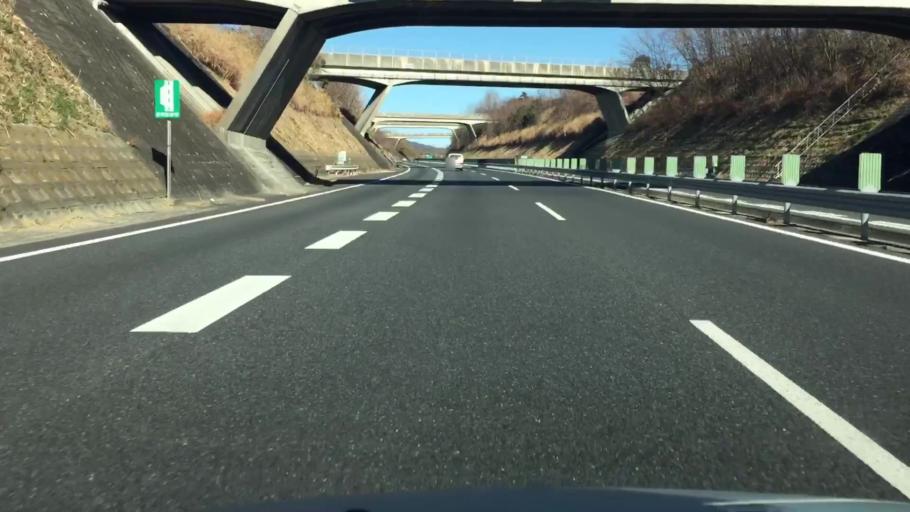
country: JP
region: Gunma
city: Shibukawa
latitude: 36.4925
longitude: 139.0311
